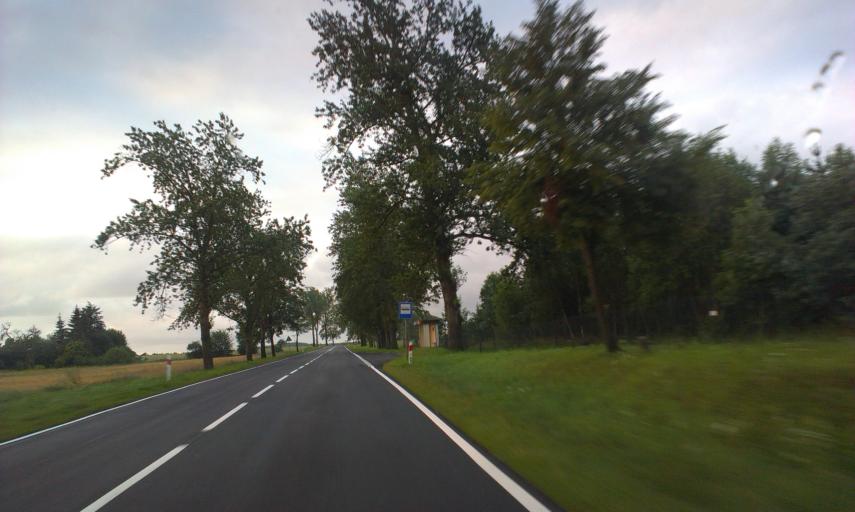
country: PL
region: Greater Poland Voivodeship
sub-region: Powiat zlotowski
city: Okonek
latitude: 53.5660
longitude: 16.8317
